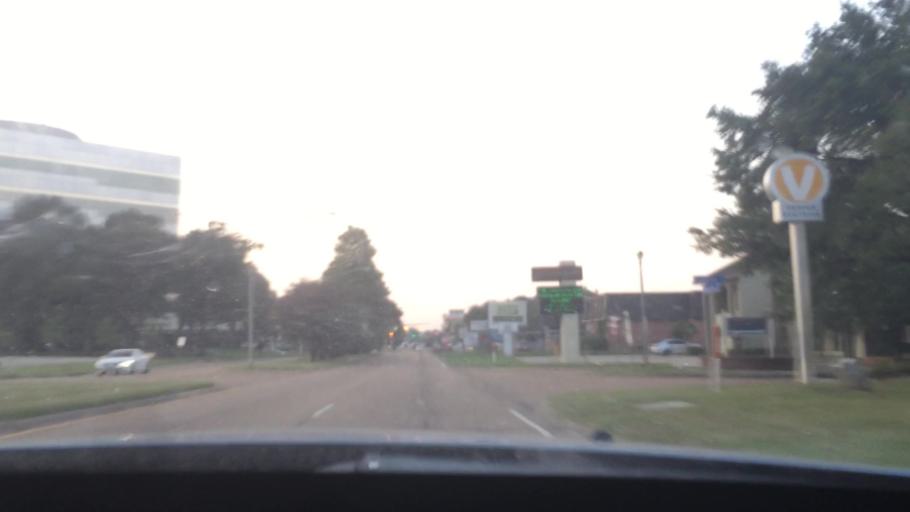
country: US
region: Louisiana
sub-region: East Baton Rouge Parish
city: Inniswold
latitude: 30.4156
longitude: -91.0515
